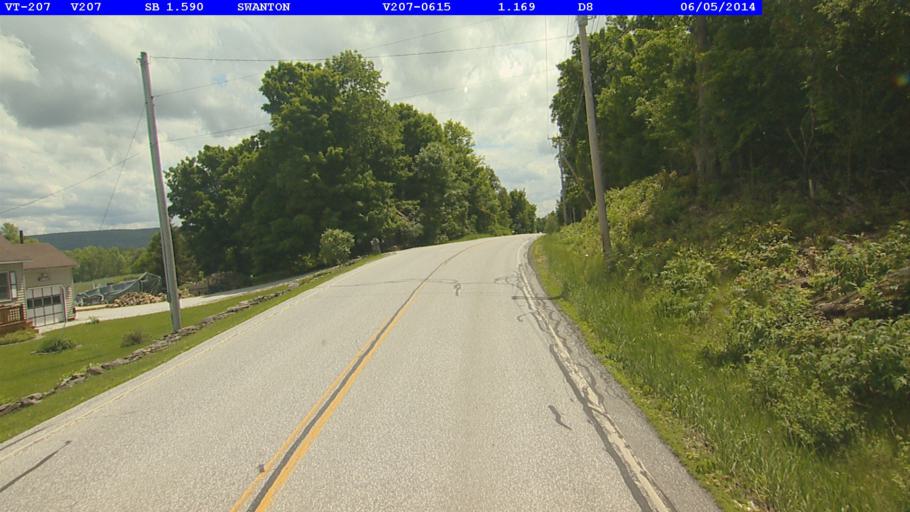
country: US
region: Vermont
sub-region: Franklin County
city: Saint Albans
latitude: 44.8620
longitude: -73.0748
